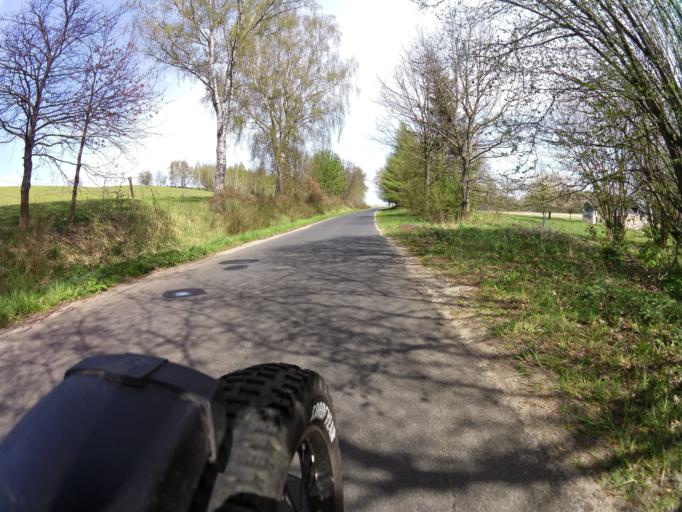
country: PL
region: West Pomeranian Voivodeship
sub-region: Powiat lobeski
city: Resko
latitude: 53.7815
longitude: 15.4187
